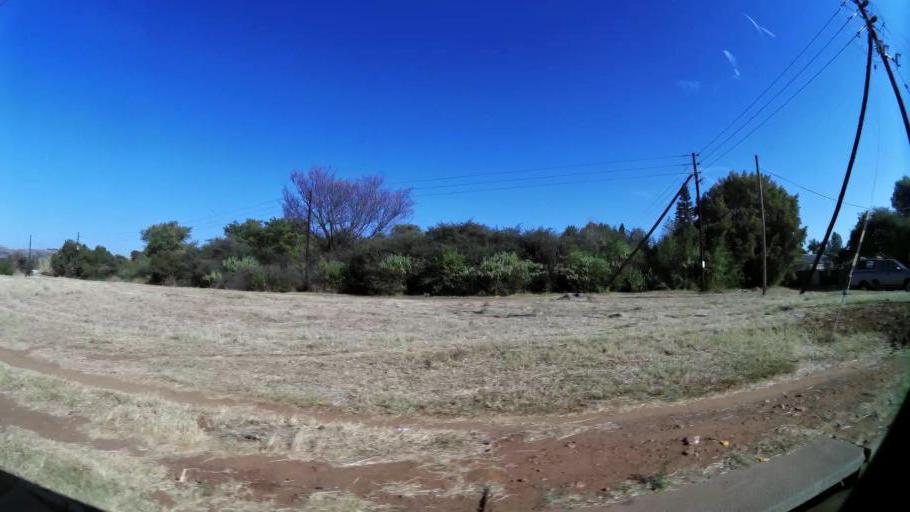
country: ZA
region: Gauteng
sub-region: City of Tshwane Metropolitan Municipality
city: Pretoria
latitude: -25.6605
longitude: 28.1319
